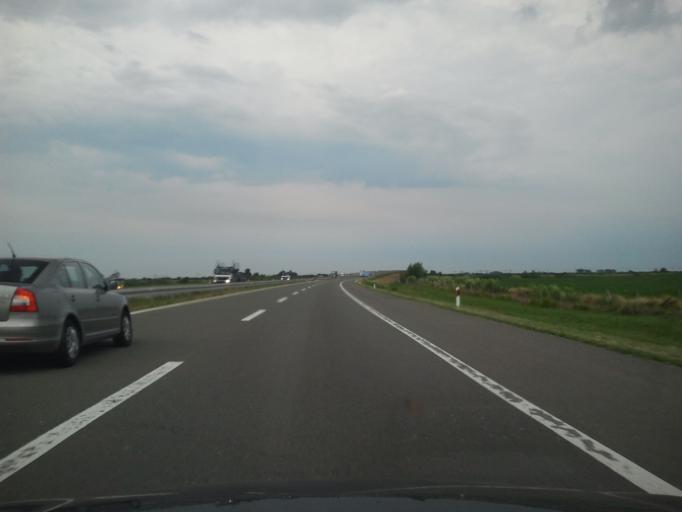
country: RS
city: Sasinci
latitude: 44.9941
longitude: 19.6991
